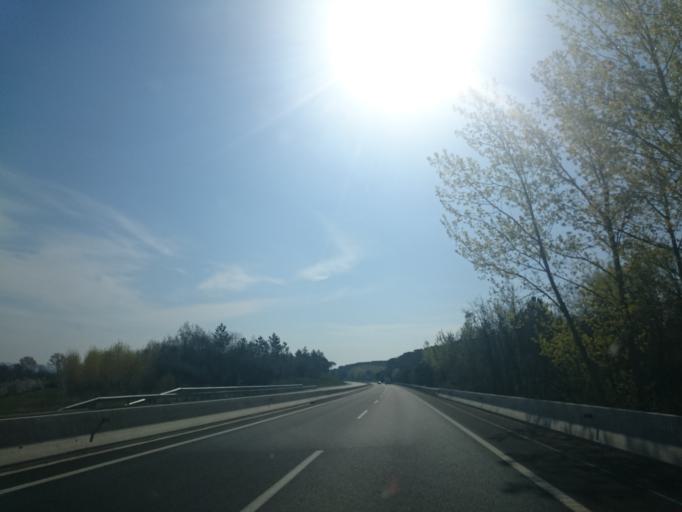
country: ES
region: Catalonia
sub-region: Provincia de Girona
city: Vilobi d'Onyar
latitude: 41.8771
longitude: 2.7399
